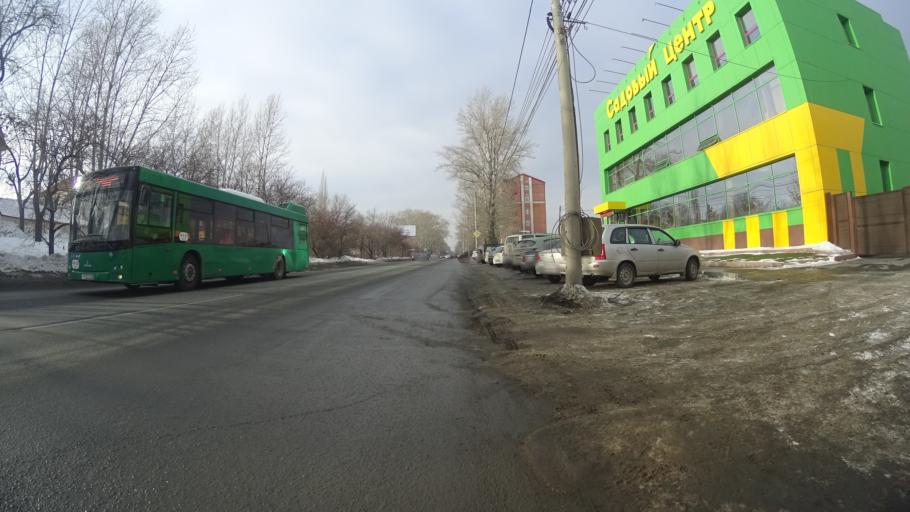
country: RU
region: Chelyabinsk
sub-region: Gorod Chelyabinsk
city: Chelyabinsk
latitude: 55.1206
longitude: 61.3797
